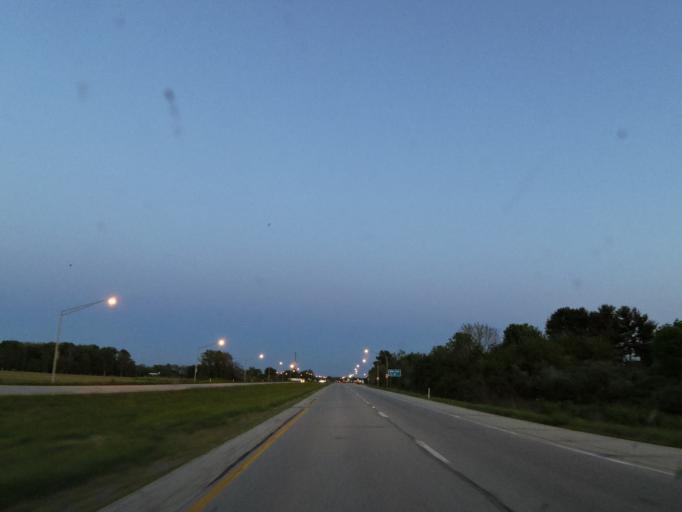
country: US
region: Indiana
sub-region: Hendricks County
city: Pittsboro
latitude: 39.9057
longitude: -86.5608
